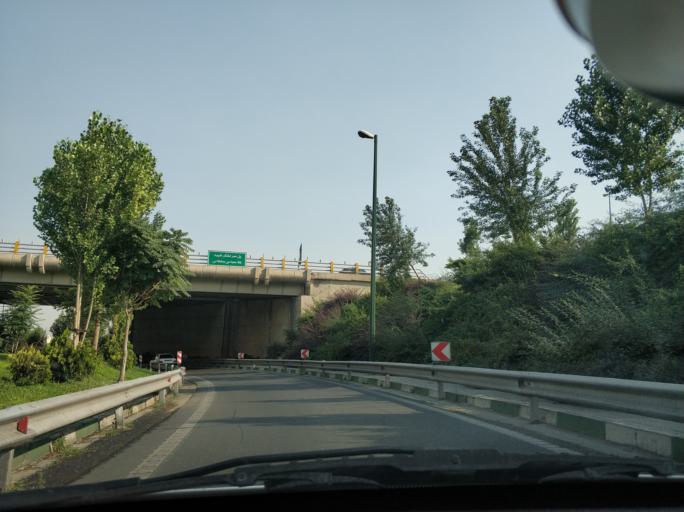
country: IR
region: Tehran
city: Tehran
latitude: 35.7401
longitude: 51.3680
